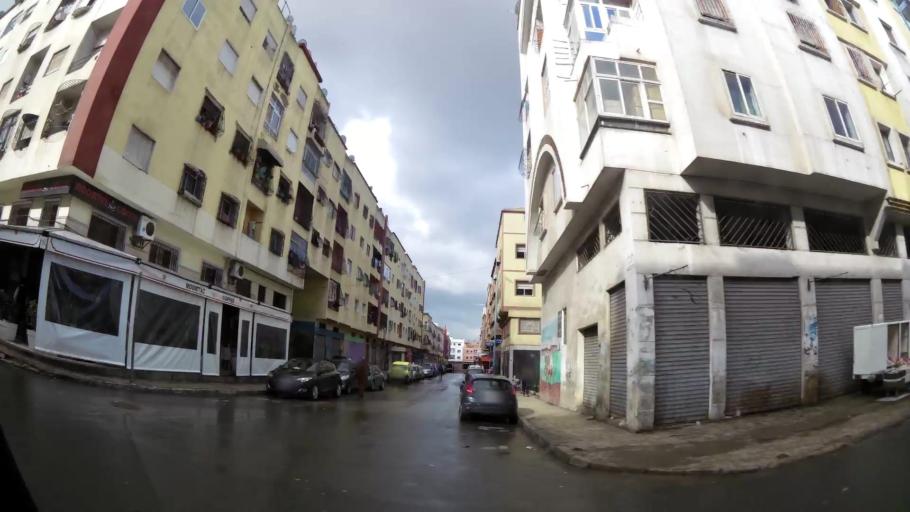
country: MA
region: Grand Casablanca
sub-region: Mediouna
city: Tit Mellil
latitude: 33.5925
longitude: -7.5173
